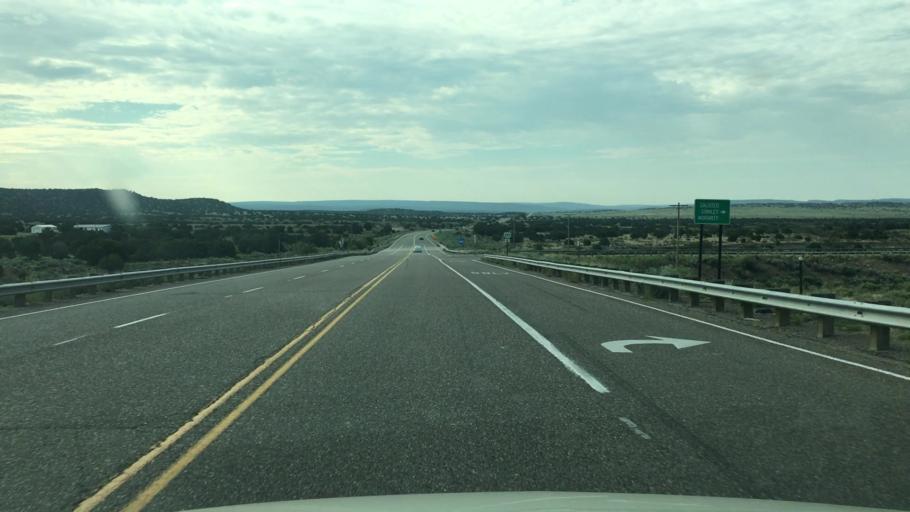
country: US
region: New Mexico
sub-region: Santa Fe County
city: Eldorado at Santa Fe
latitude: 35.4645
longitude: -105.8993
